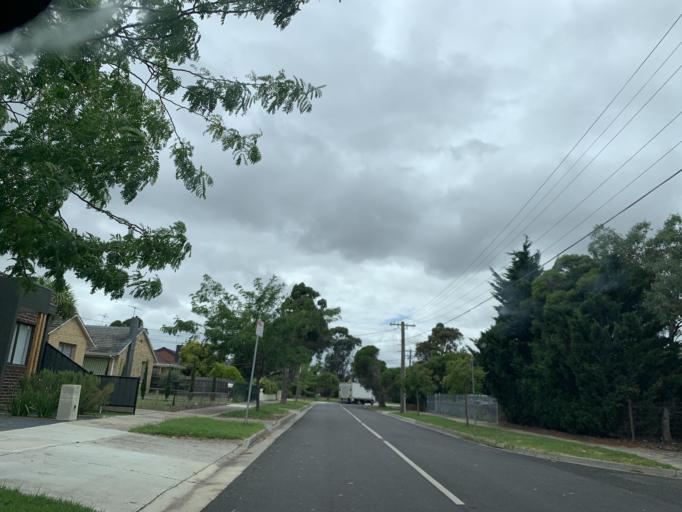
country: AU
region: Victoria
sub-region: Hume
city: Jacana
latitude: -37.6864
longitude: 144.9106
